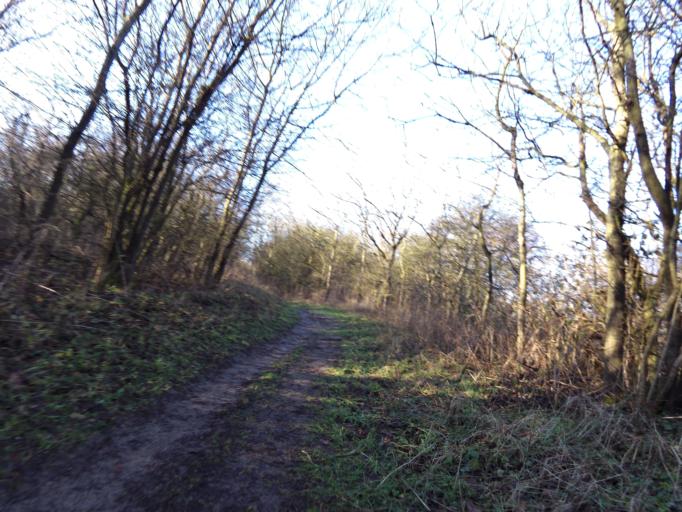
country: NL
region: South Holland
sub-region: Gemeente Rotterdam
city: Hoek van Holland
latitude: 51.9152
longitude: 4.0686
